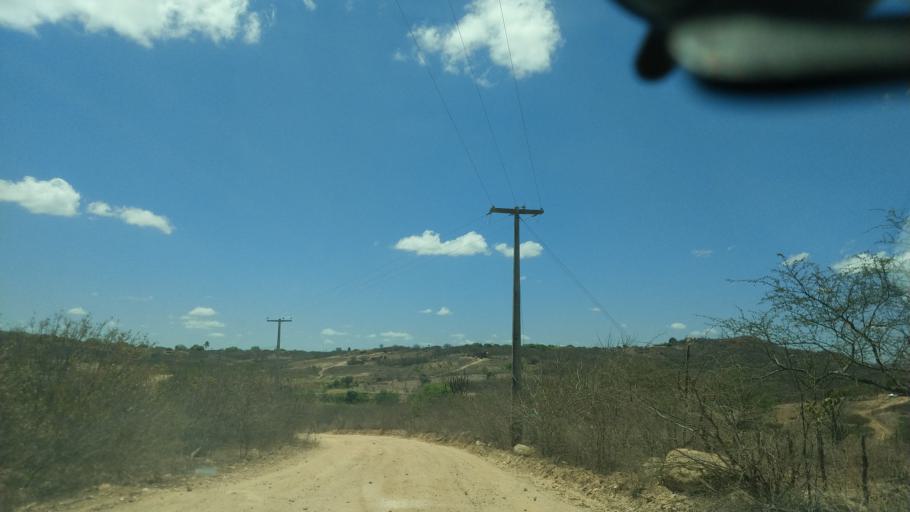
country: BR
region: Rio Grande do Norte
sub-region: Cerro Cora
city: Cerro Cora
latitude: -6.0186
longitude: -36.3309
